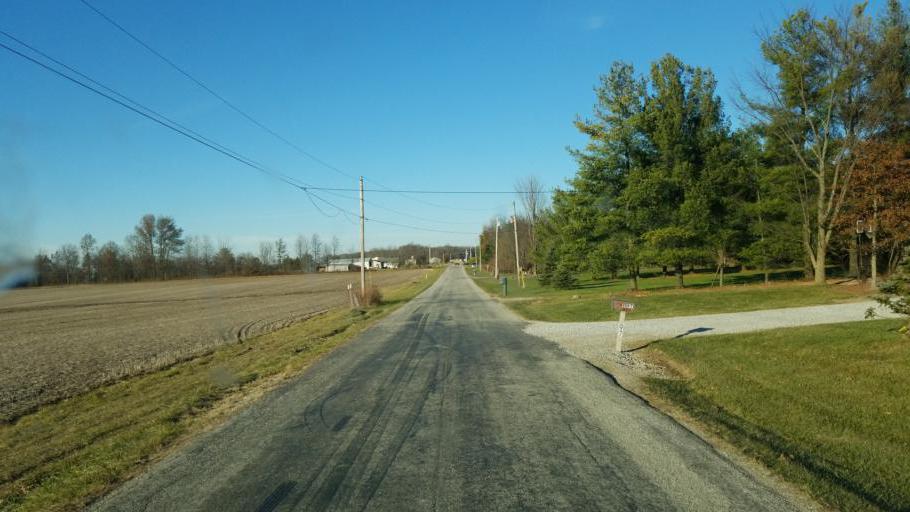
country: US
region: Ohio
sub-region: Delaware County
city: Ashley
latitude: 40.3993
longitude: -82.8831
